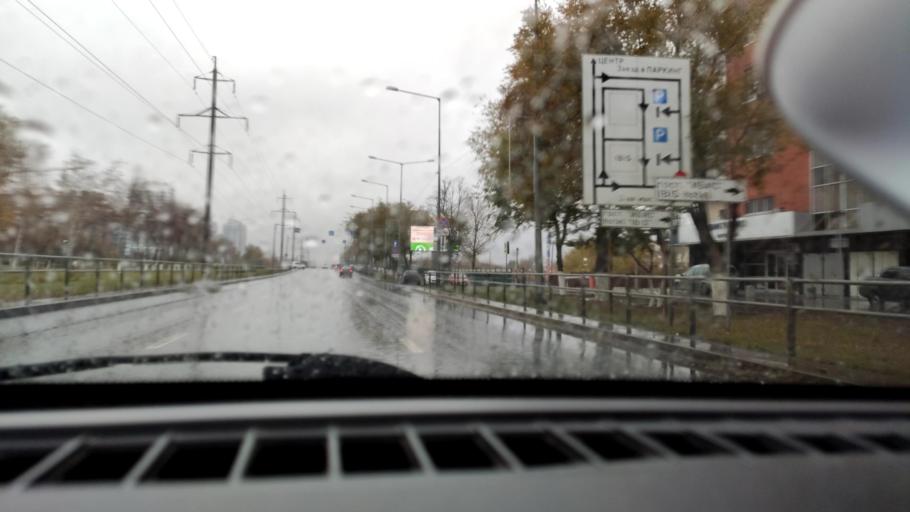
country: RU
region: Samara
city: Samara
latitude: 53.2305
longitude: 50.1785
